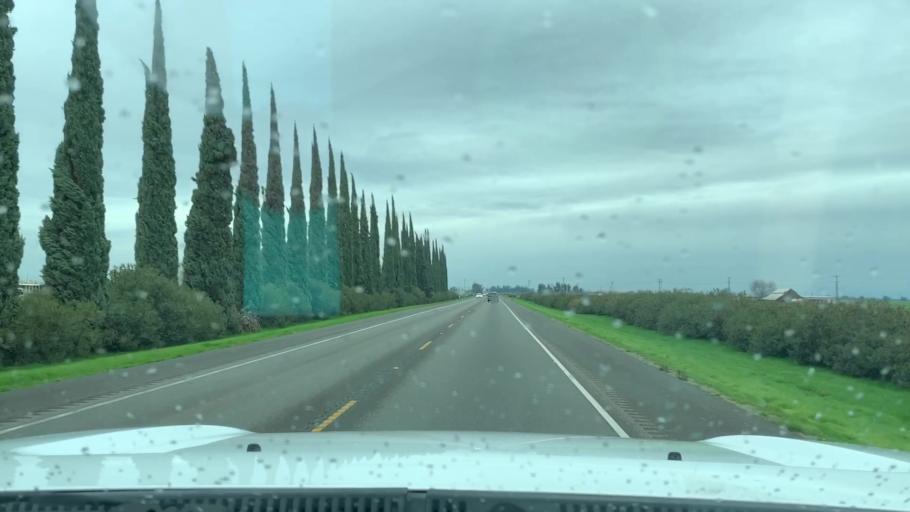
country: US
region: California
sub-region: Fresno County
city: Riverdale
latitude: 36.4351
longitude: -119.8003
